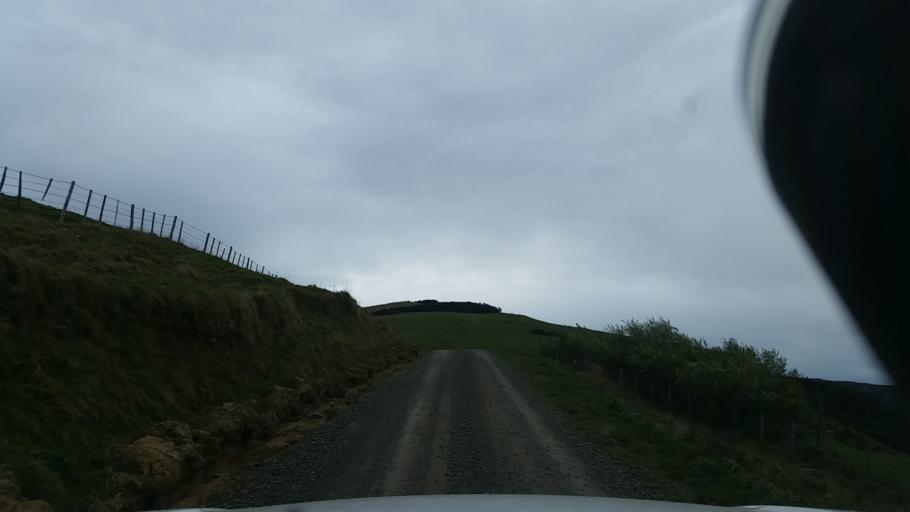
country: NZ
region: Canterbury
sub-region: Christchurch City
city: Christchurch
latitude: -43.8196
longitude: 173.0695
